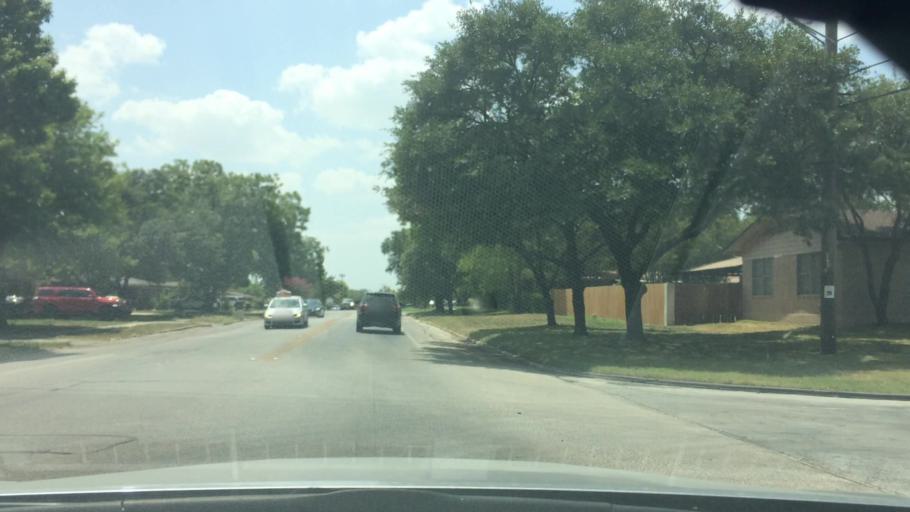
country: US
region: Texas
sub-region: Bexar County
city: Olmos Park
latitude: 29.5043
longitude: -98.4855
